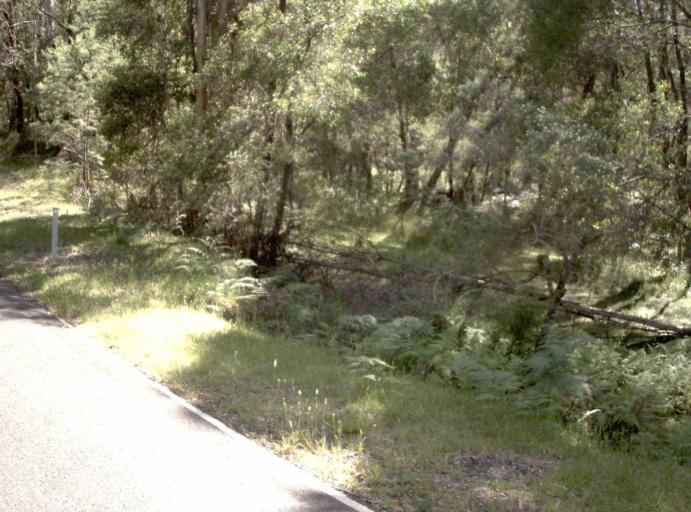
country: AU
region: New South Wales
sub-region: Bombala
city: Bombala
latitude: -37.3625
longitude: 148.6840
